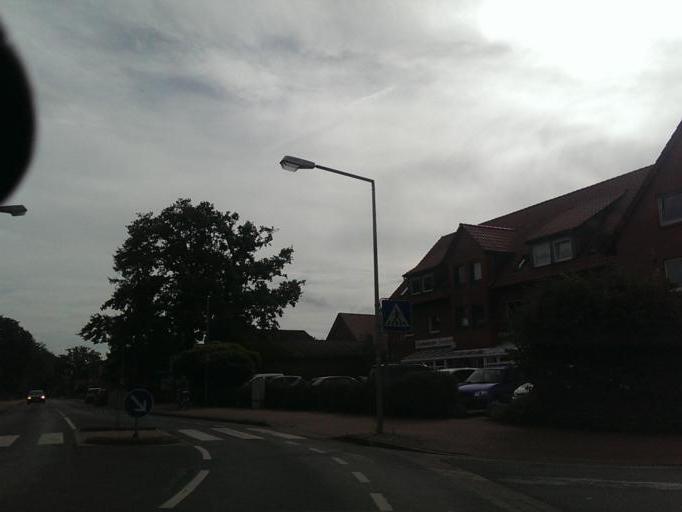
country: DE
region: Lower Saxony
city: Garbsen-Mitte
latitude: 52.4592
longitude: 9.5627
